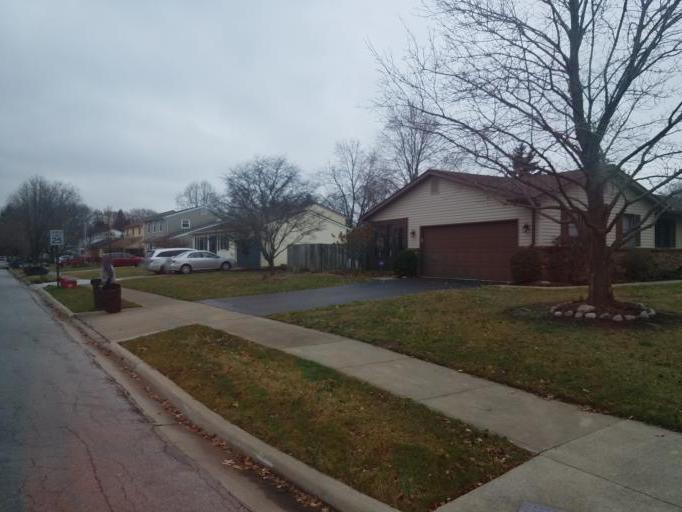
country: US
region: Ohio
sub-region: Franklin County
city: Westerville
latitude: 40.1306
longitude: -82.9683
